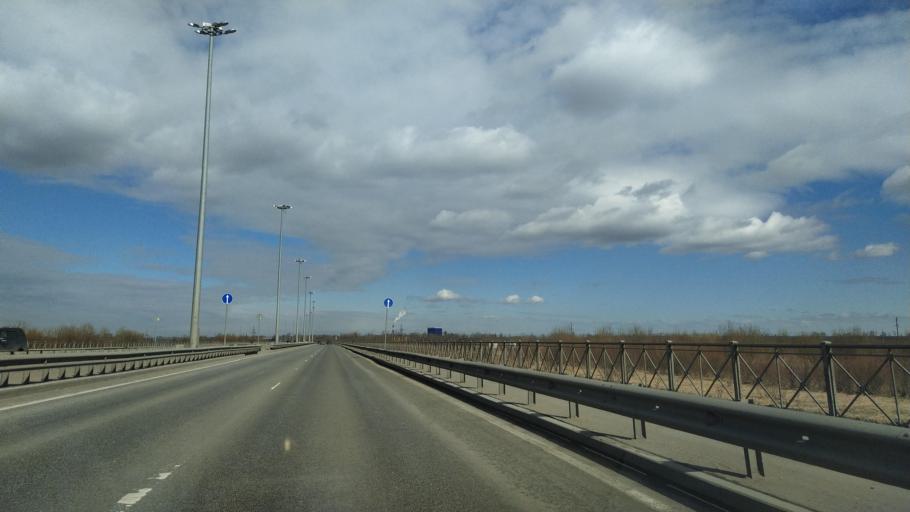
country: RU
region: St.-Petersburg
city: Shushary
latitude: 59.7645
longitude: 30.3984
